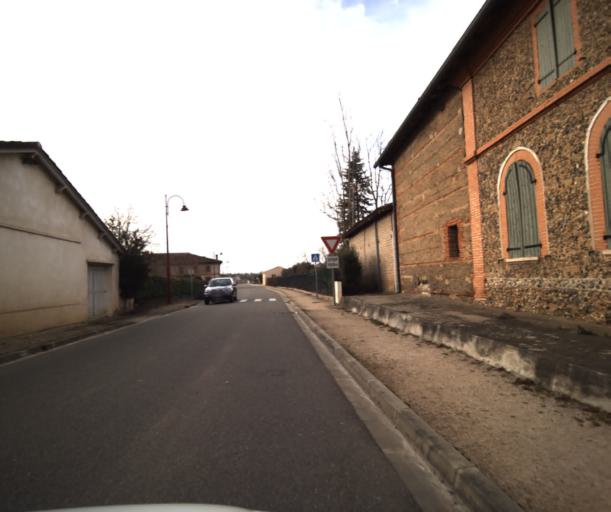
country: FR
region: Midi-Pyrenees
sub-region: Departement du Tarn-et-Garonne
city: Campsas
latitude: 43.8981
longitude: 1.3239
